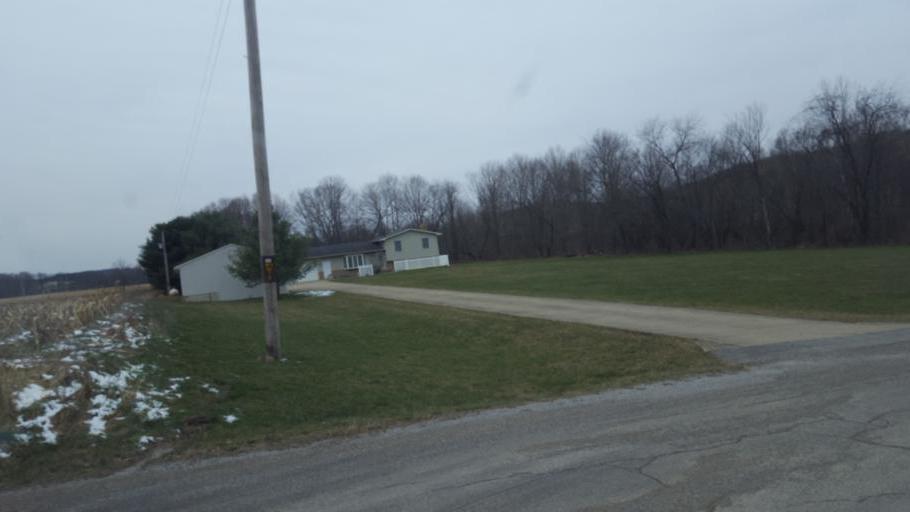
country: US
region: Ohio
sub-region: Sandusky County
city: Bellville
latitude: 40.5948
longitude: -82.4905
